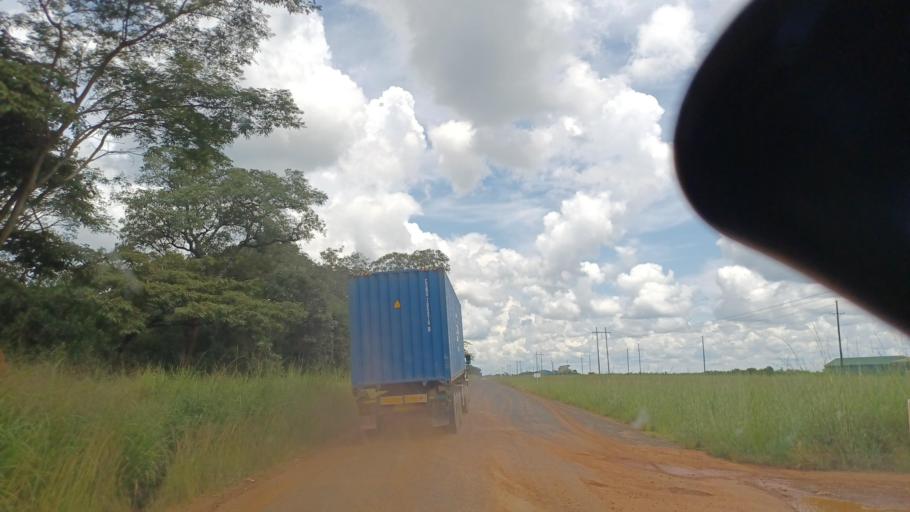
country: ZM
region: North-Western
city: Solwezi
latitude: -12.4384
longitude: 26.2097
